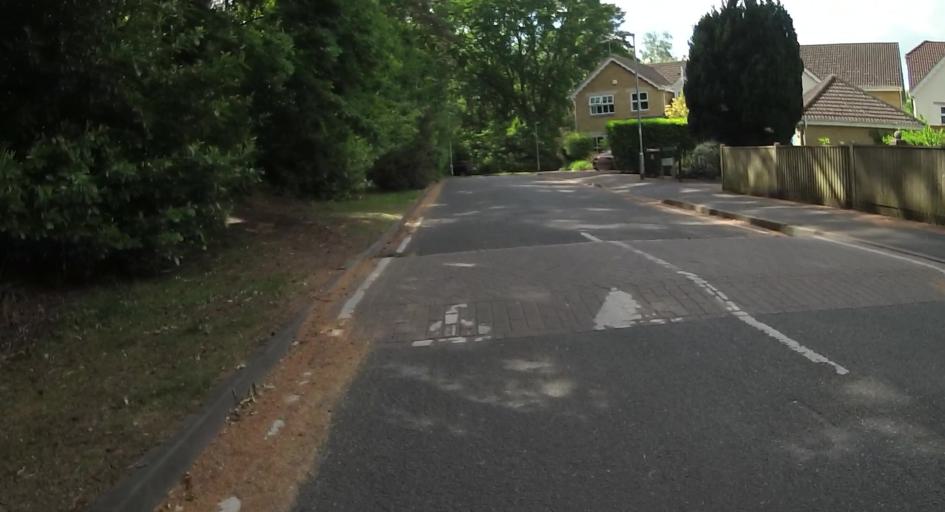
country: GB
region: England
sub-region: Bracknell Forest
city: Crowthorne
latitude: 51.3813
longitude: -0.7995
